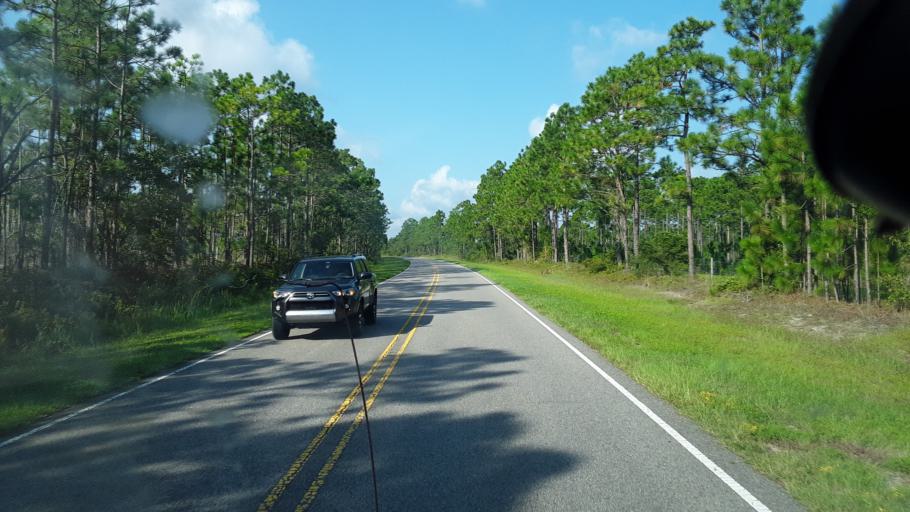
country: US
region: North Carolina
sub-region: Brunswick County
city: Boiling Spring Lakes
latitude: 34.0505
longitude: -77.9951
